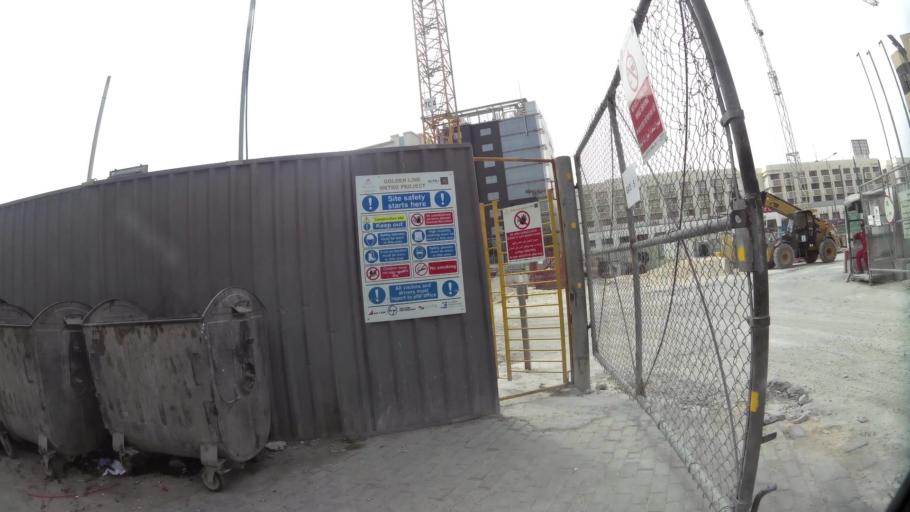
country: QA
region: Baladiyat ad Dawhah
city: Doha
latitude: 25.2813
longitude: 51.4968
